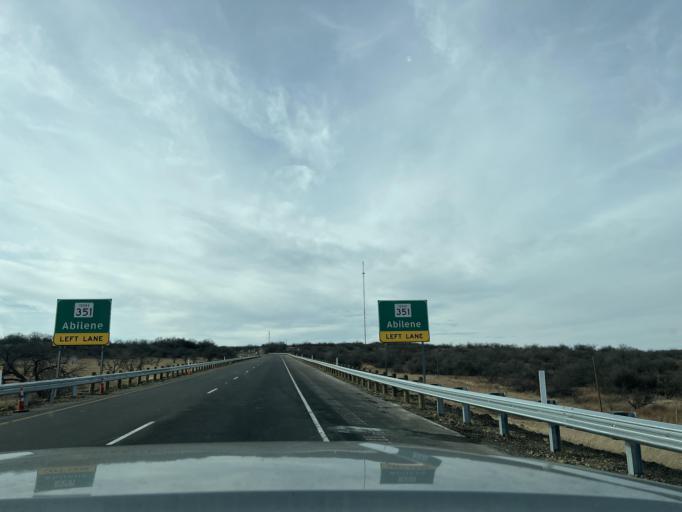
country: US
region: Texas
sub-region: Shackelford County
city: Albany
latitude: 32.7065
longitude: -99.4134
